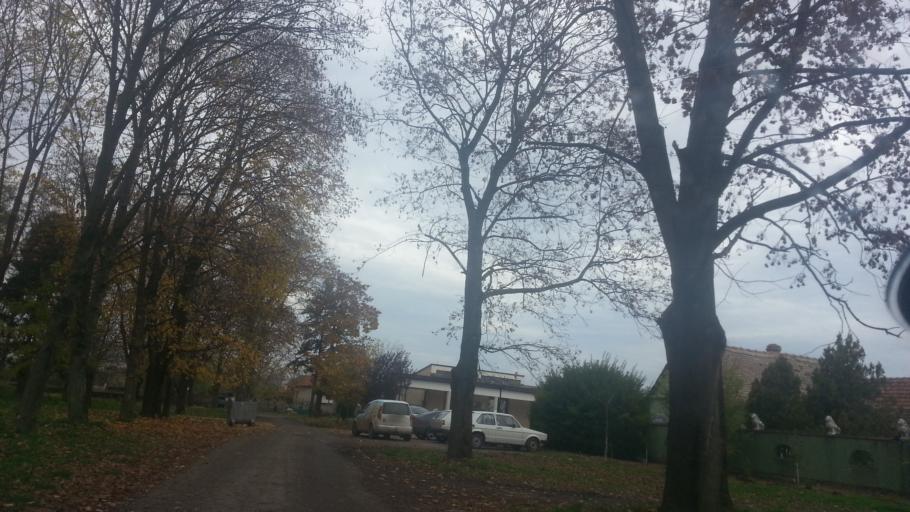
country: RS
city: Golubinci
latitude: 44.9911
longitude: 20.0689
